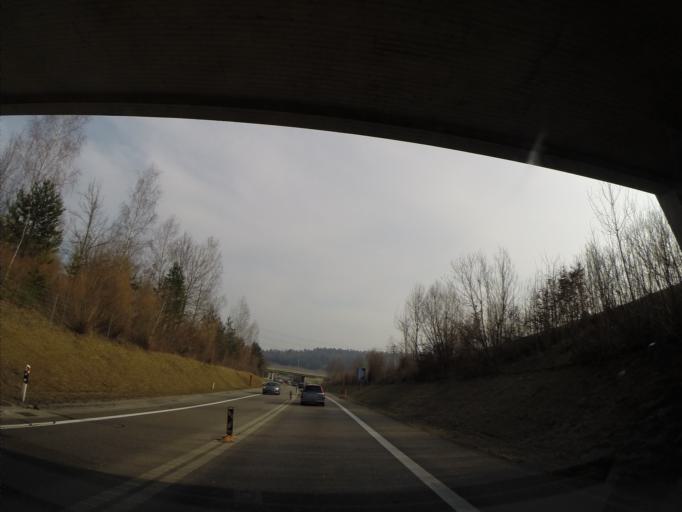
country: CH
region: Zurich
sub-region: Bezirk Winterthur
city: Wuelflingen (Kreis 6) / Lindenplatz
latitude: 47.5290
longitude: 8.6962
